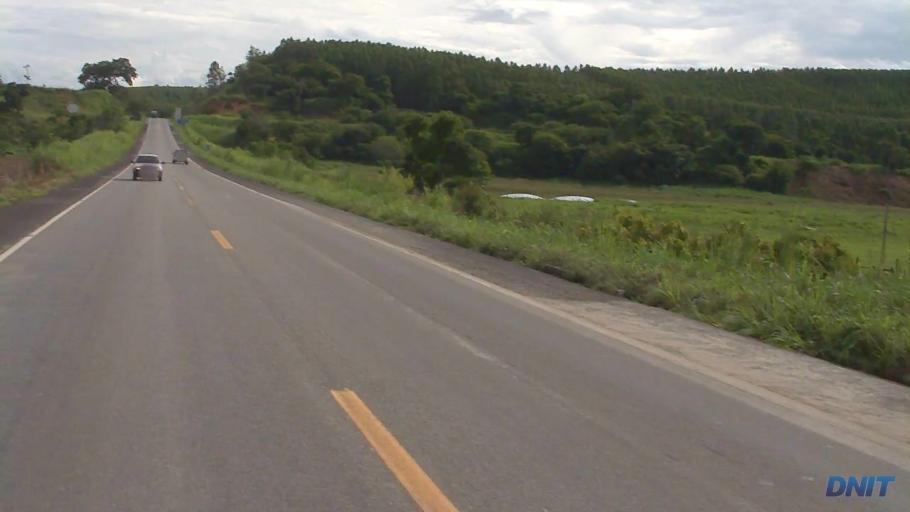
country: BR
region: Minas Gerais
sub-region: Belo Oriente
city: Belo Oriente
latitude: -19.2422
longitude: -42.3353
